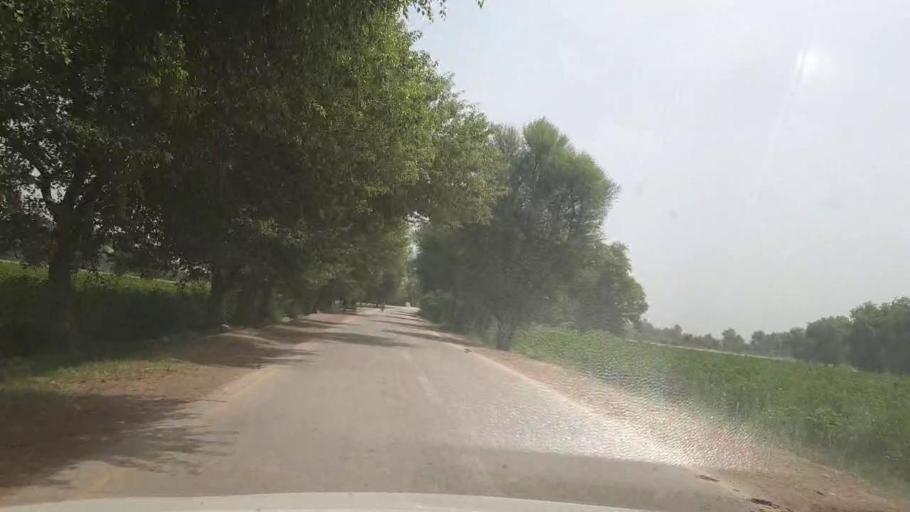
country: PK
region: Sindh
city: Kot Diji
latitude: 27.3735
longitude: 68.6506
